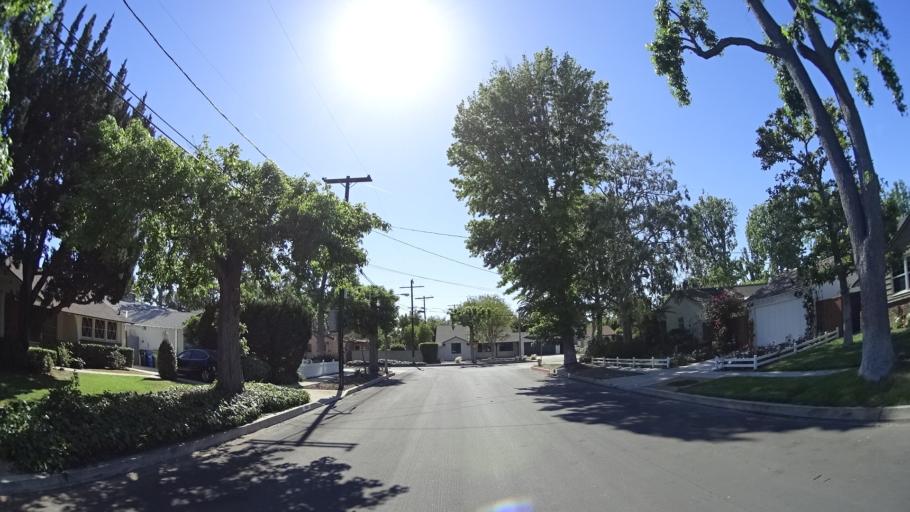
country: US
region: California
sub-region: Los Angeles County
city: Sherman Oaks
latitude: 34.1667
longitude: -118.4178
